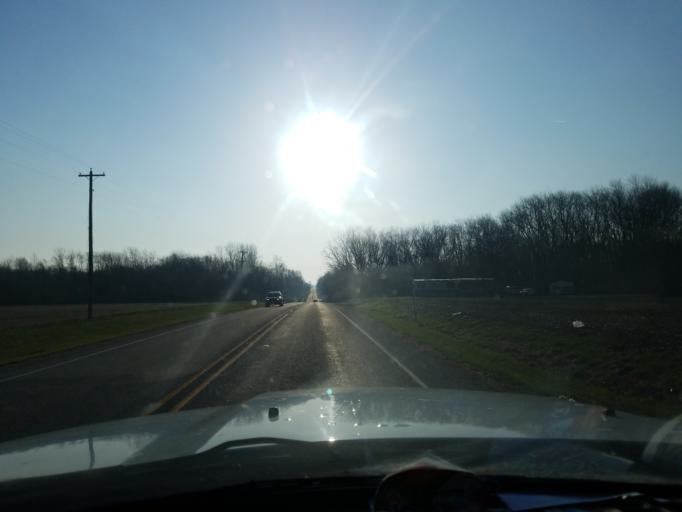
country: US
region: Indiana
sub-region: Vigo County
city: Seelyville
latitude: 39.3903
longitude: -87.2668
